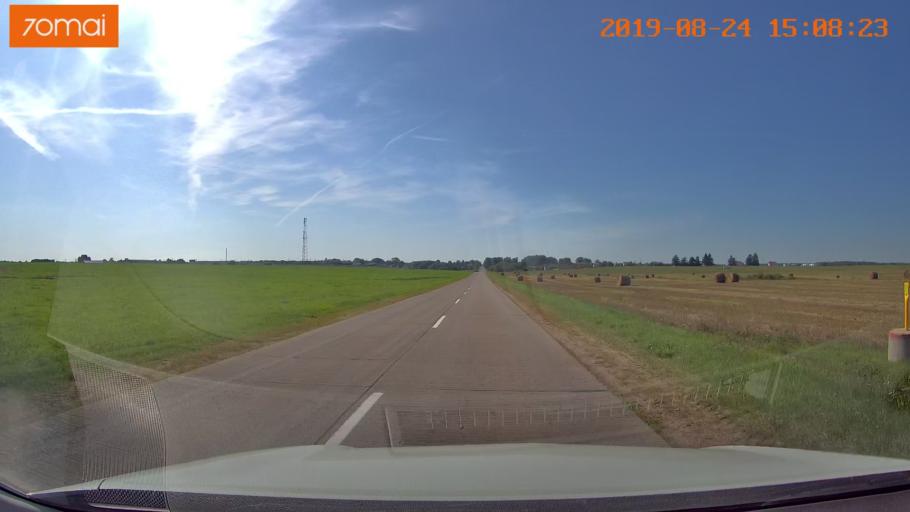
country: BY
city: Michanovichi
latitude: 53.6085
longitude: 27.6584
